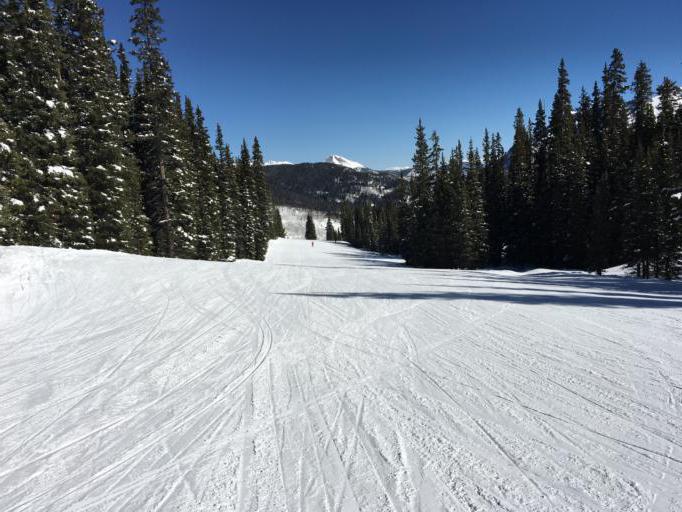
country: US
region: Colorado
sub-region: Summit County
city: Frisco
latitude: 39.4820
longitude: -106.1619
